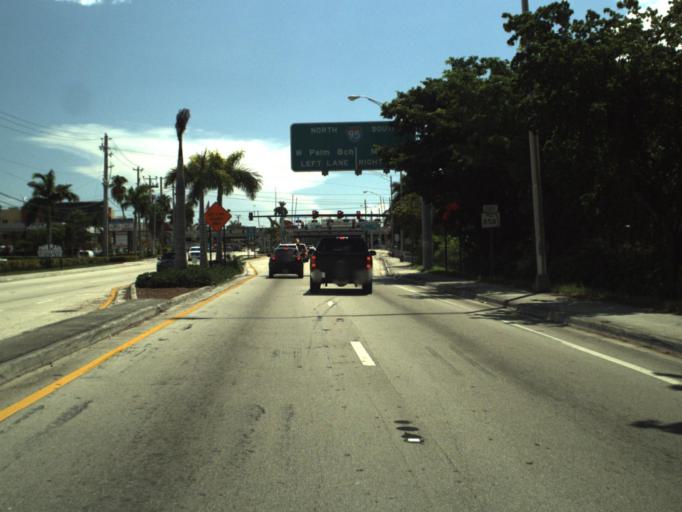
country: US
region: Florida
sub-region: Broward County
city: Pembroke Park
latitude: 25.9848
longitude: -80.1692
